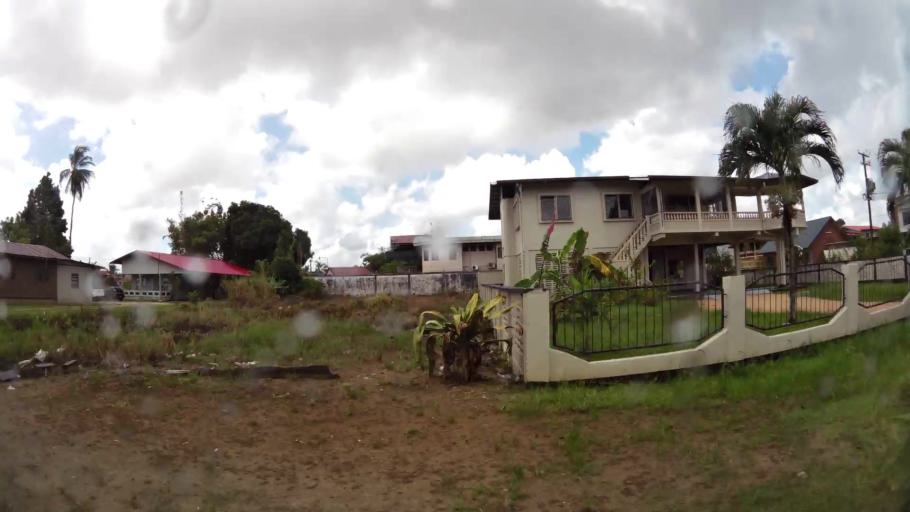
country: SR
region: Paramaribo
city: Paramaribo
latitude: 5.8334
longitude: -55.2162
